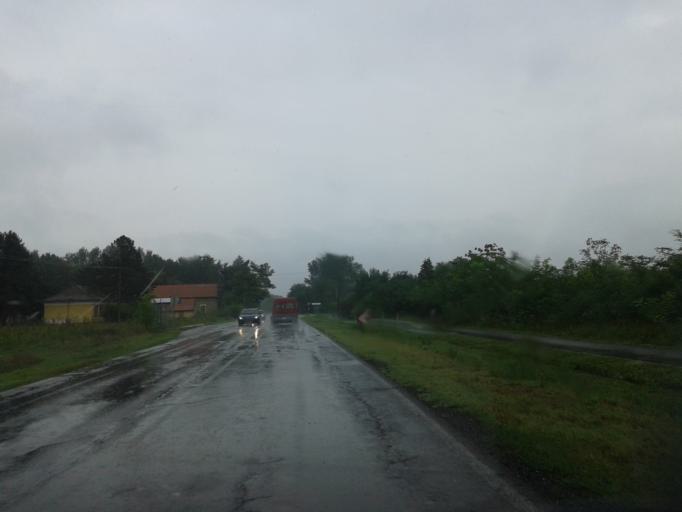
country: HU
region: Csongrad
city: Asotthalom
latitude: 46.2220
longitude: 19.8138
